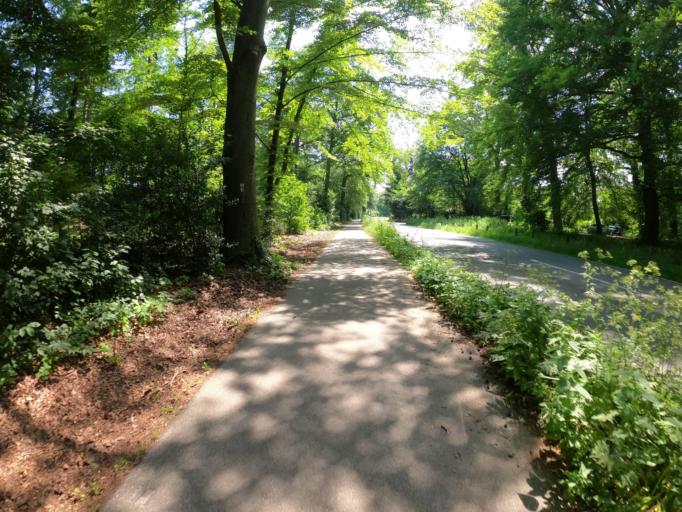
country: DE
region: North Rhine-Westphalia
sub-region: Regierungsbezirk Dusseldorf
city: Hunxe
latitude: 51.7108
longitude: 6.7781
